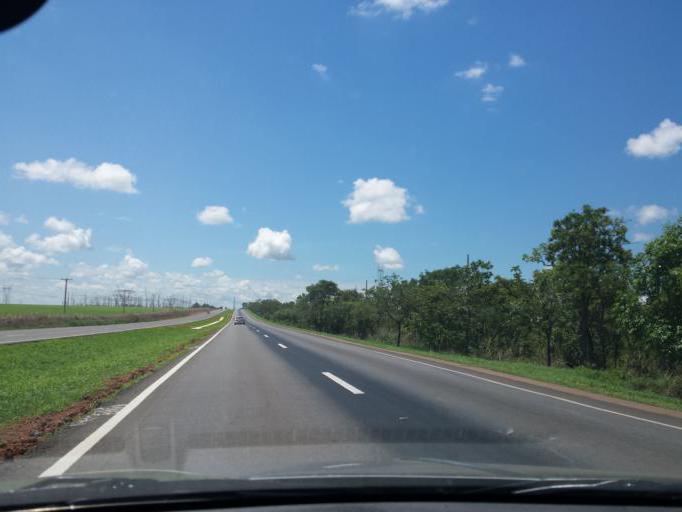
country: BR
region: Goias
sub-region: Luziania
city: Luziania
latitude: -16.3353
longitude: -47.8371
